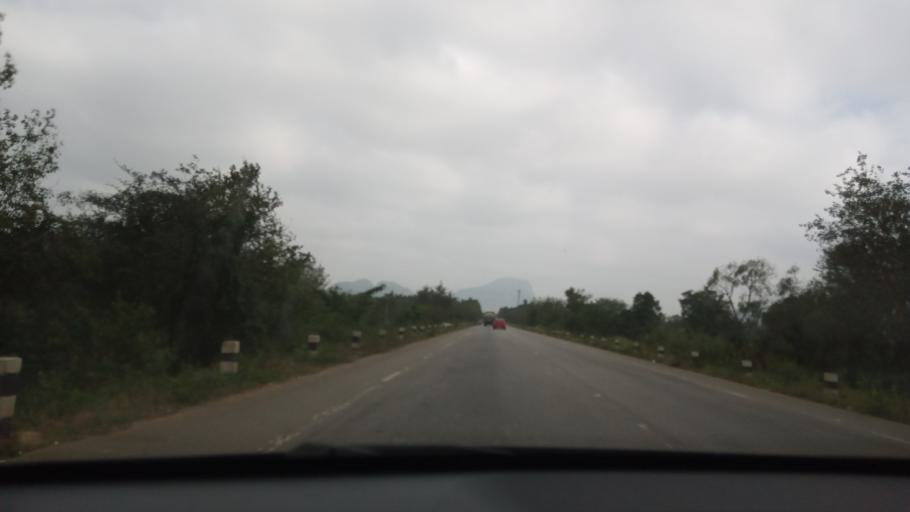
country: IN
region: Karnataka
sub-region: Chikkaballapur
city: Chintamani
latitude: 13.3086
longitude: 77.9759
